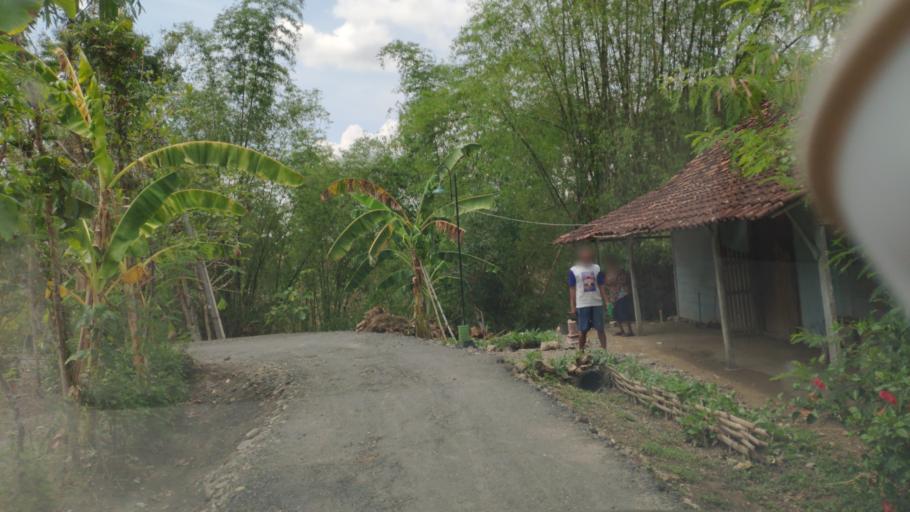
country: ID
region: Central Java
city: Mojo Wetan
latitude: -7.0299
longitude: 111.3742
